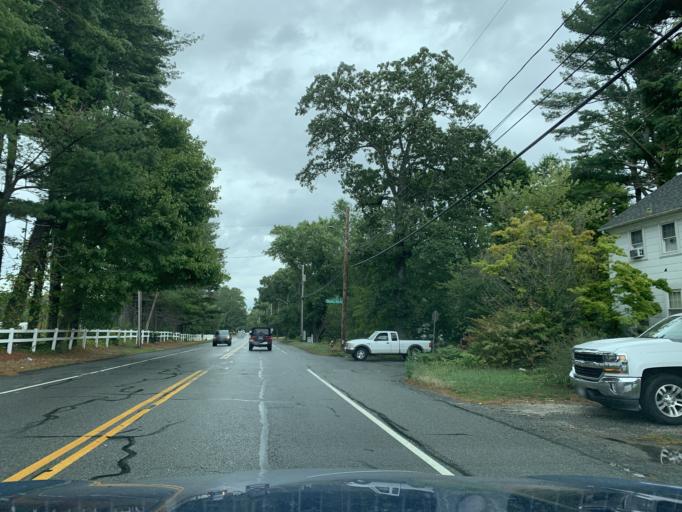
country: US
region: Rhode Island
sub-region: Bristol County
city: Warren
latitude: 41.7617
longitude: -71.2692
